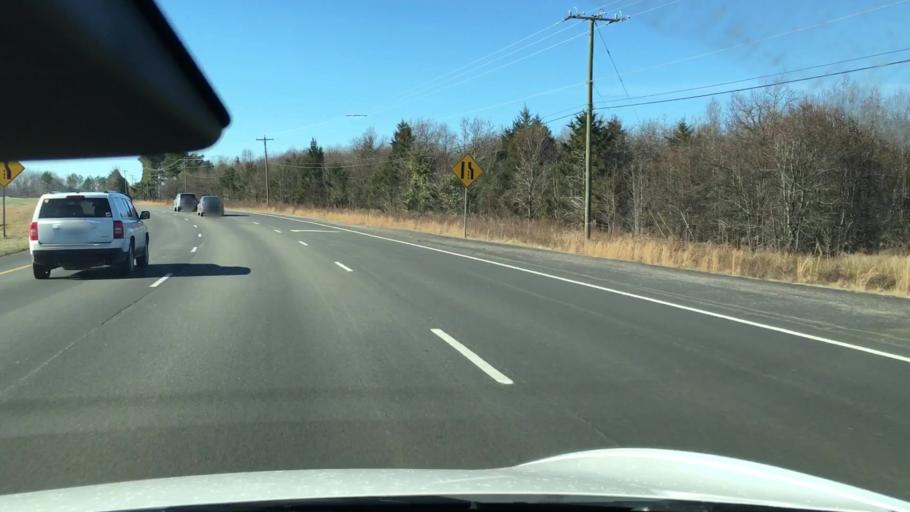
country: US
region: Virginia
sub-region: Chesterfield County
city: Woodlake
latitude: 37.5076
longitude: -77.6990
